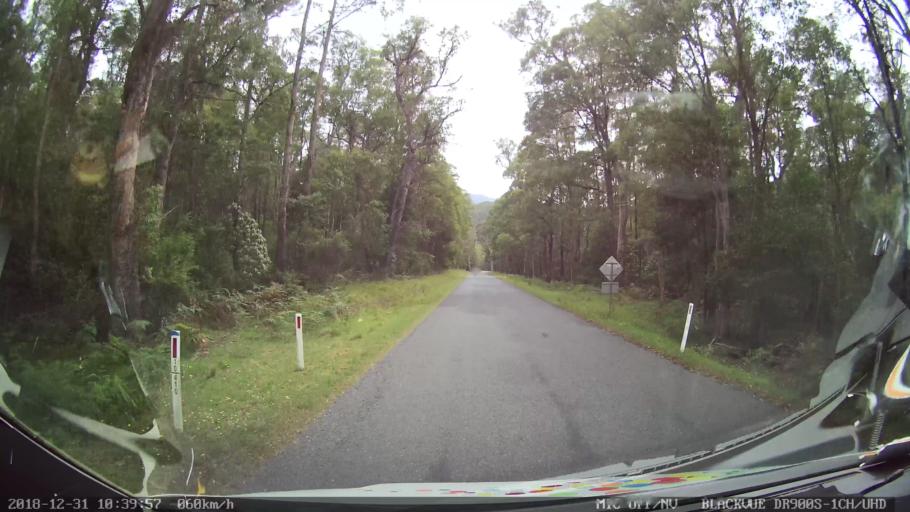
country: AU
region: New South Wales
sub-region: Snowy River
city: Jindabyne
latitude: -36.3939
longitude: 148.1780
